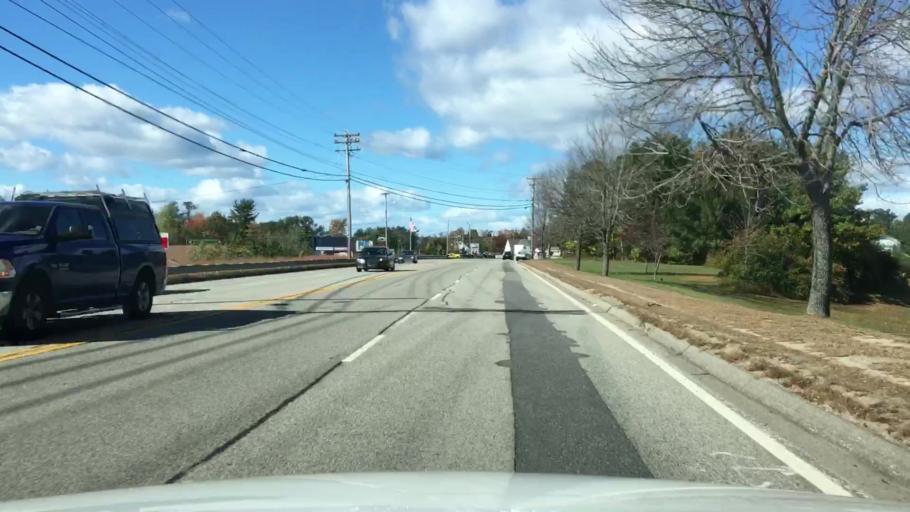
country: US
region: Maine
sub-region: York County
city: South Sanford
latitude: 43.4129
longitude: -70.7454
